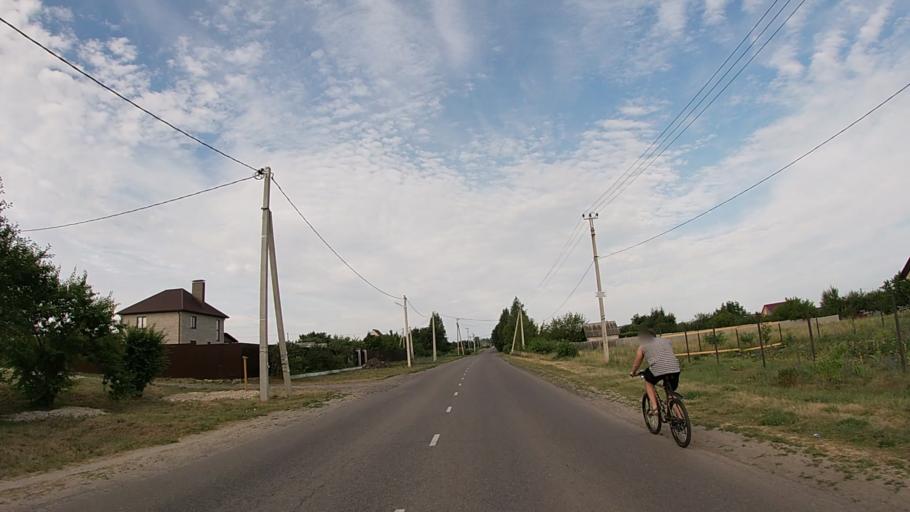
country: RU
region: Belgorod
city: Severnyy
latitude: 50.6941
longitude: 36.5694
